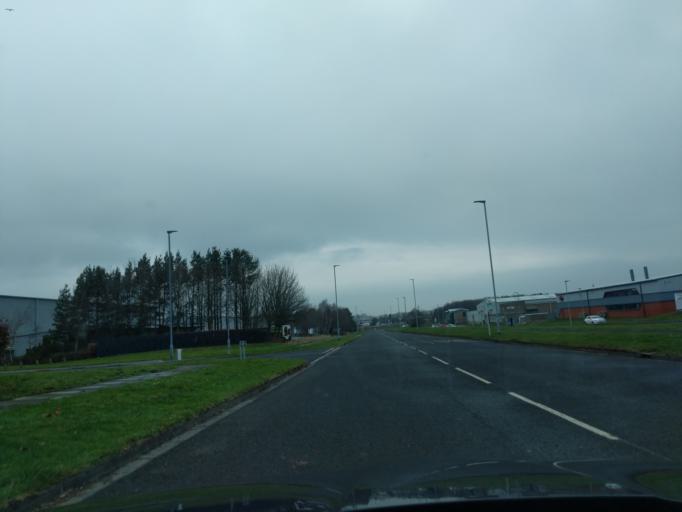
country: GB
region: England
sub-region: Northumberland
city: Cramlington
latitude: 55.0976
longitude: -1.6100
